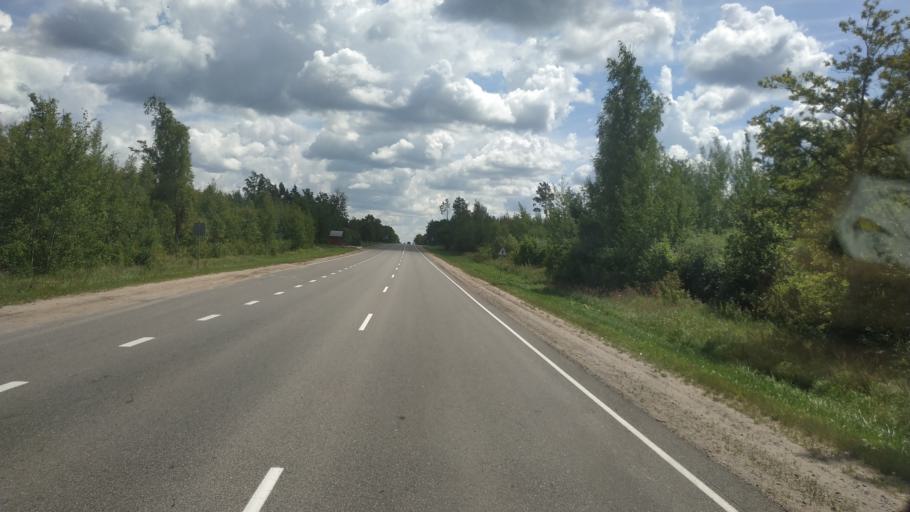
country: BY
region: Mogilev
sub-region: Mahilyowski Rayon
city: Veyno
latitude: 53.8221
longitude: 30.4306
